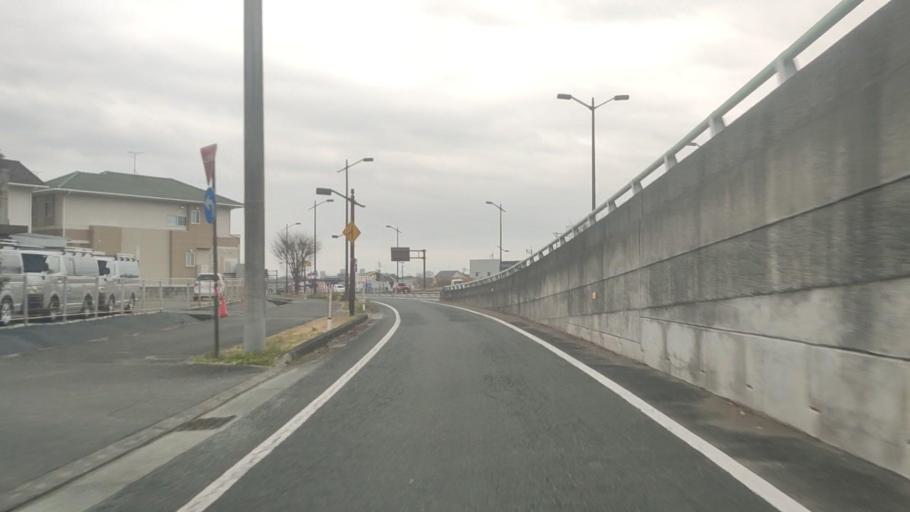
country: JP
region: Kumamoto
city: Ozu
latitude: 32.8250
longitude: 130.7914
